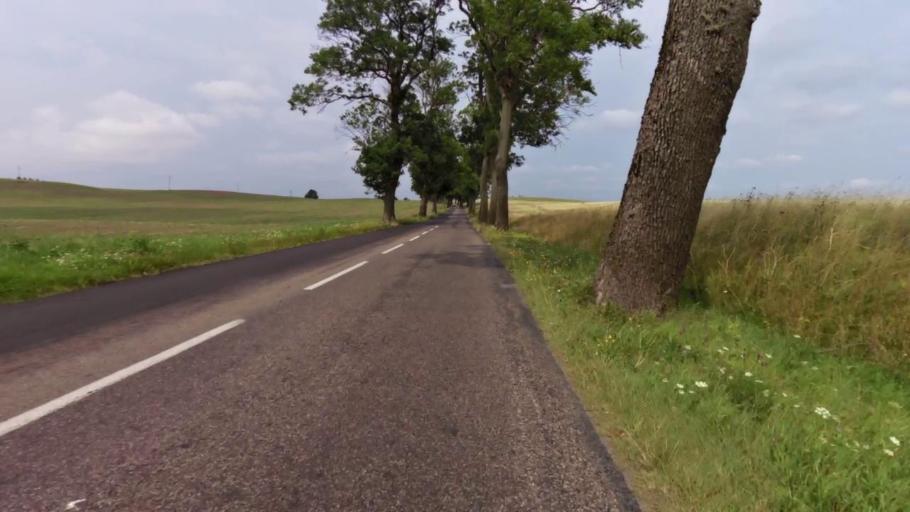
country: PL
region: West Pomeranian Voivodeship
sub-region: Powiat drawski
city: Drawsko Pomorskie
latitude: 53.5573
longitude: 15.8272
